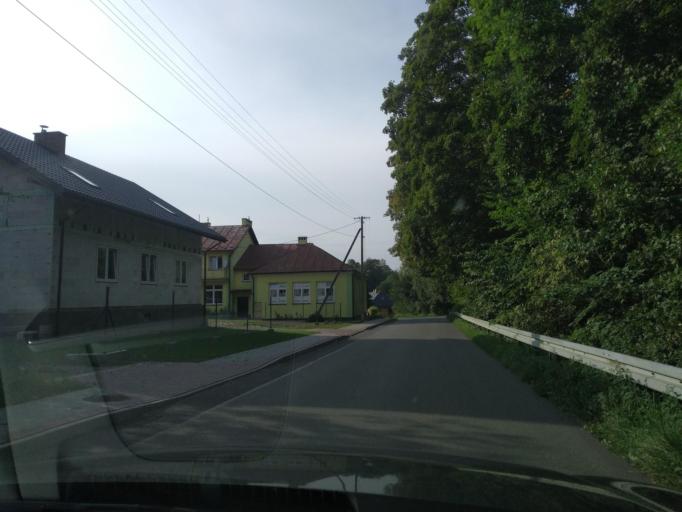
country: PL
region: Subcarpathian Voivodeship
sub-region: Powiat brzozowski
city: Dydnia
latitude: 49.6628
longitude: 22.1958
